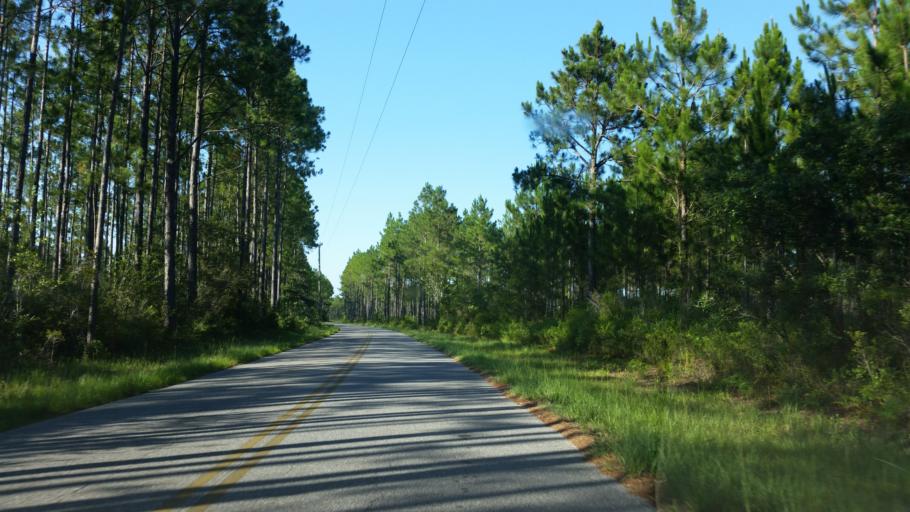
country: US
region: Florida
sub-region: Escambia County
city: Bellview
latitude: 30.4748
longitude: -87.3970
